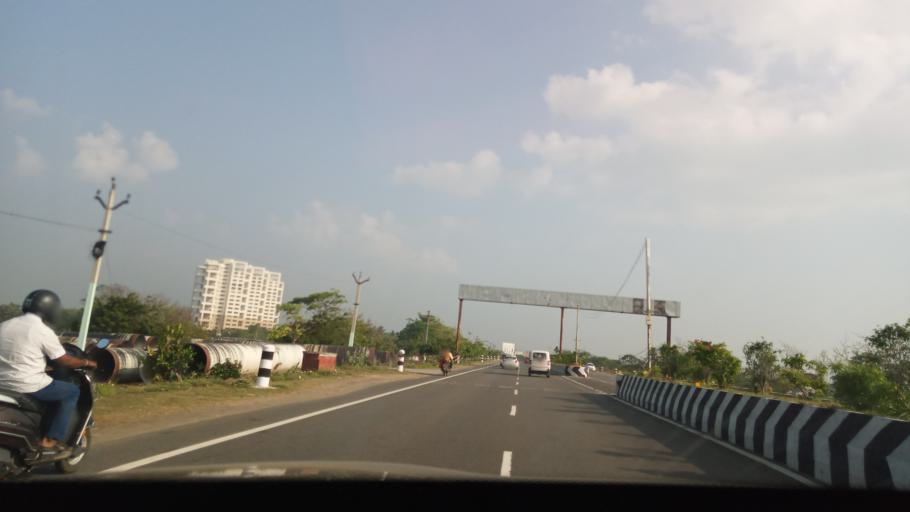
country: IN
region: Tamil Nadu
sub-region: Kancheepuram
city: Injambakkam
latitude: 12.7692
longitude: 80.2476
